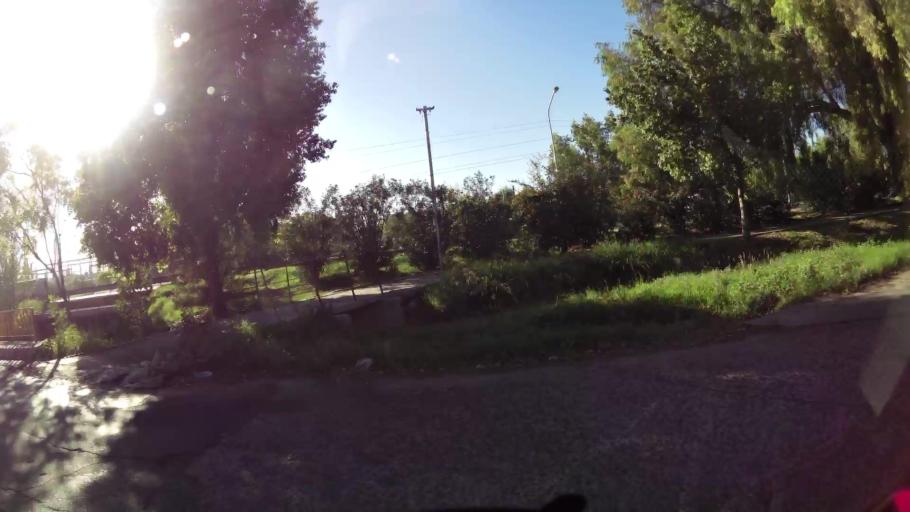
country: AR
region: Mendoza
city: Las Heras
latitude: -32.8638
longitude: -68.8107
